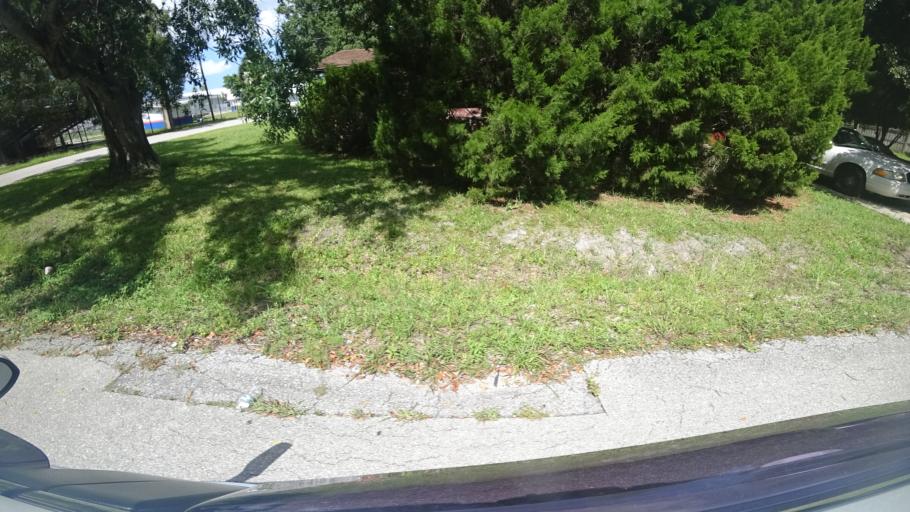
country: US
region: Florida
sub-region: Manatee County
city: Samoset
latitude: 27.4698
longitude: -82.5491
